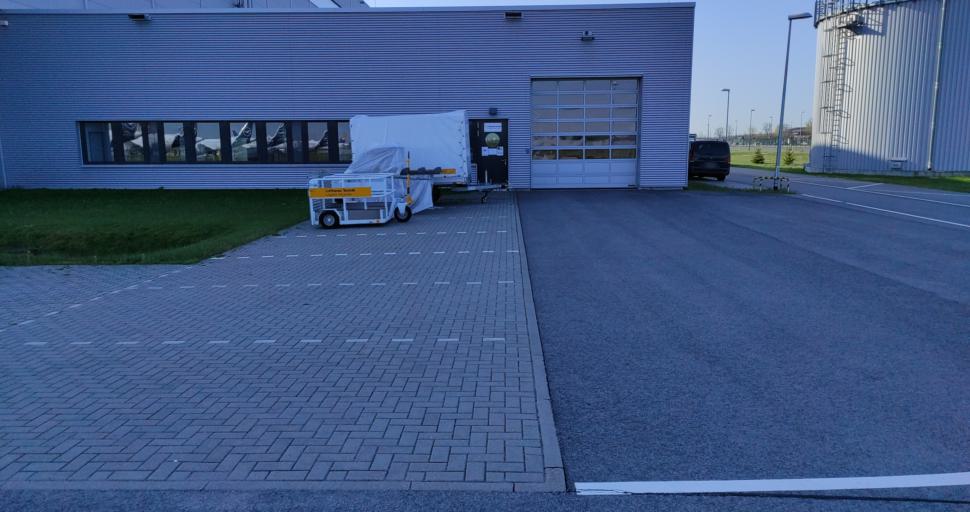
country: DE
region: Brandenburg
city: Schonefeld
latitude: 52.3597
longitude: 13.4809
